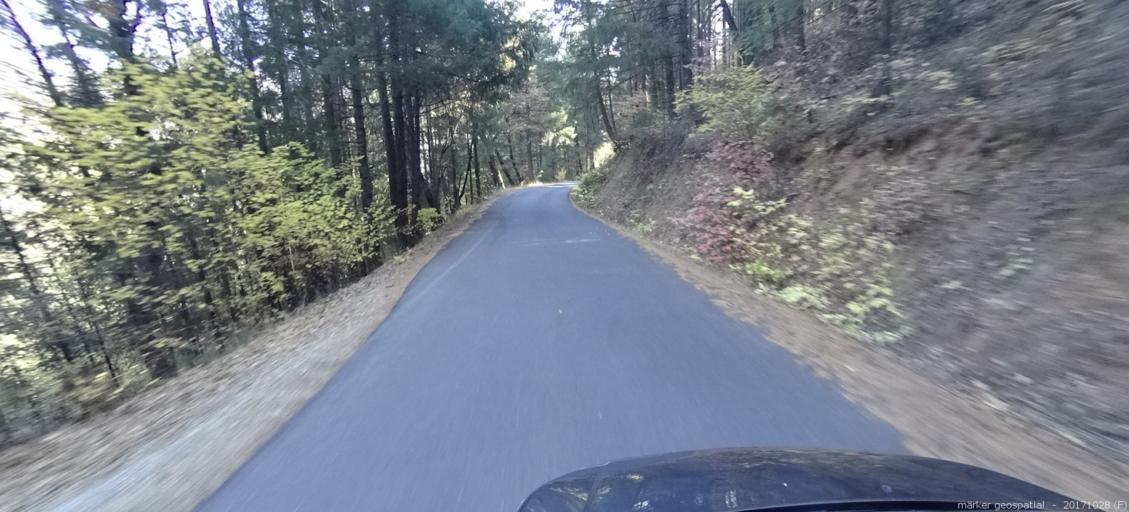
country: US
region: California
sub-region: Trinity County
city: Lewiston
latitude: 40.8097
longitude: -122.6184
